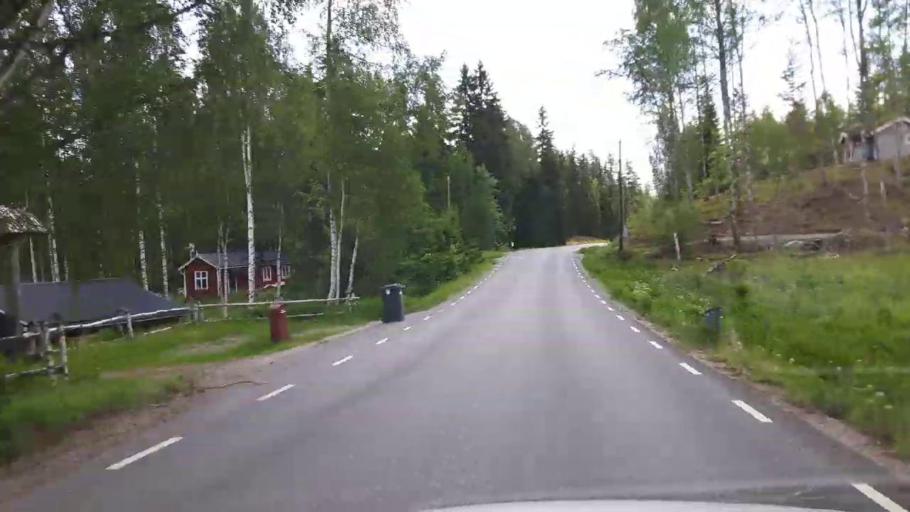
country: SE
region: Dalarna
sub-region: Faluns Kommun
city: Falun
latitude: 60.6624
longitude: 15.7615
